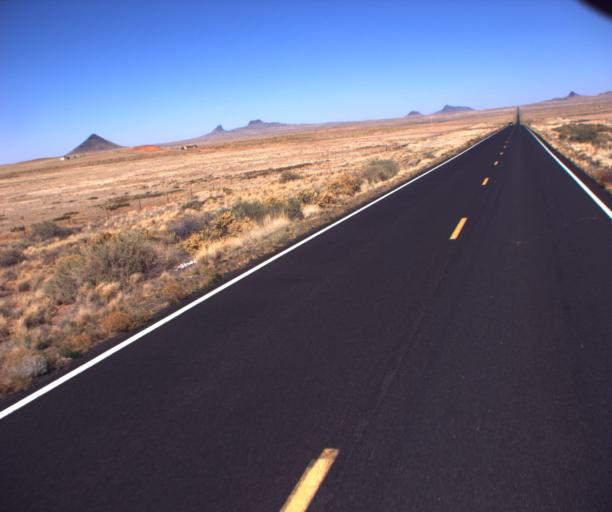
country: US
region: Arizona
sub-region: Navajo County
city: Dilkon
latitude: 35.3162
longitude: -110.4229
